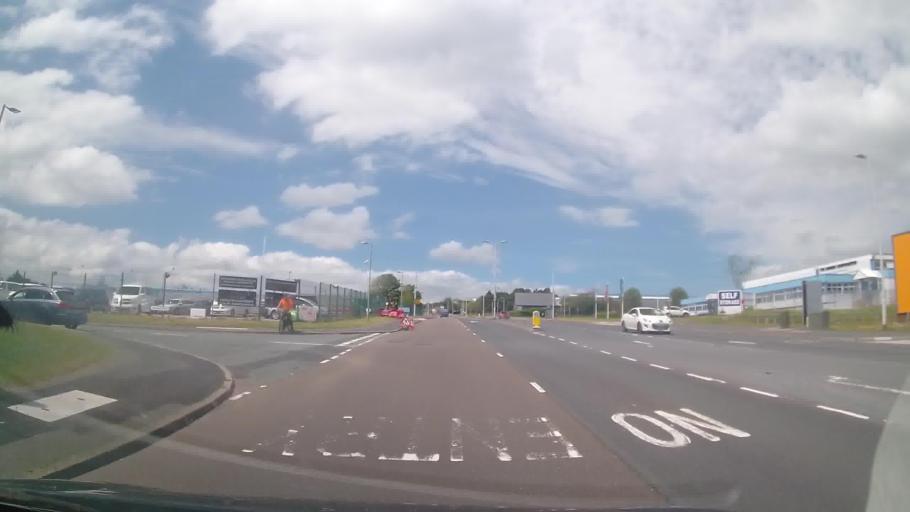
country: GB
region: England
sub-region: Devon
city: Plympton
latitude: 50.4183
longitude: -4.0925
